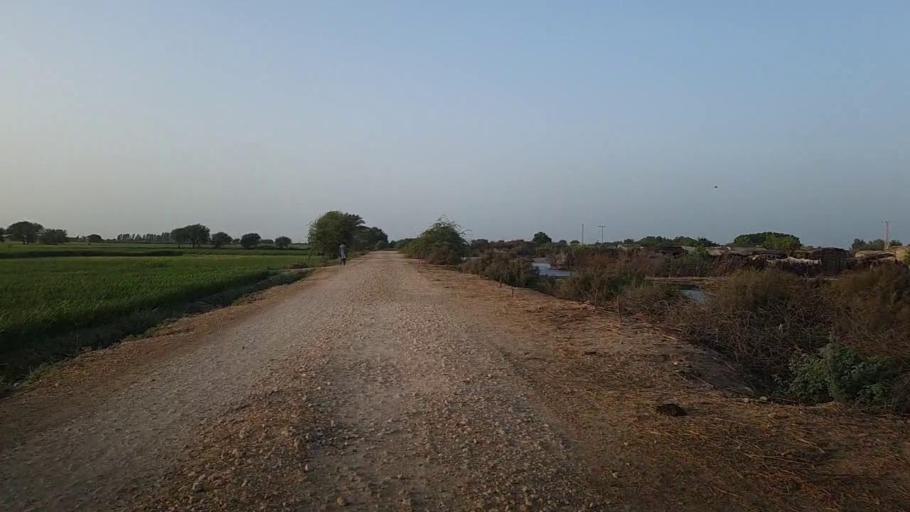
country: PK
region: Sindh
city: Kario
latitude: 24.7167
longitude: 68.4621
